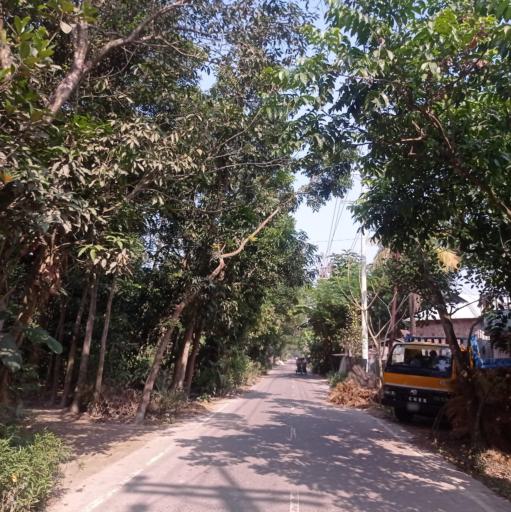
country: BD
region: Dhaka
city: Narsingdi
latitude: 24.0395
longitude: 90.6774
